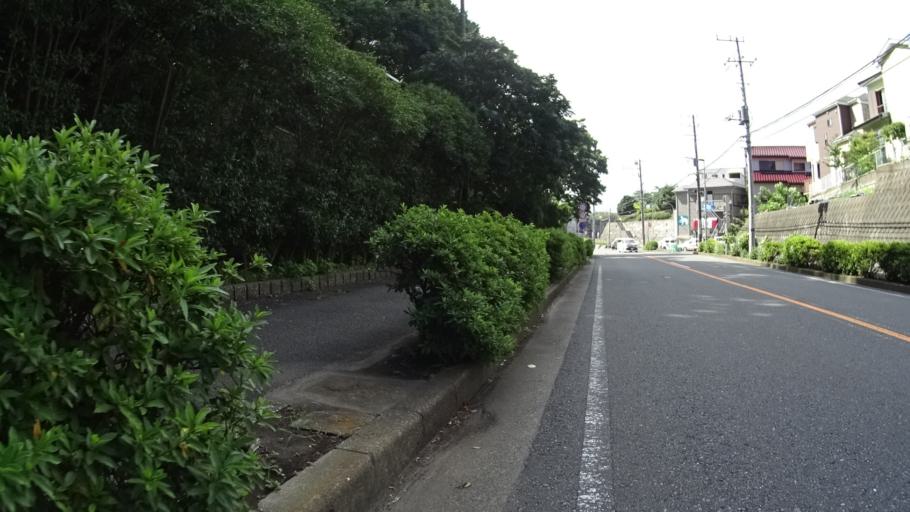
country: JP
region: Kanagawa
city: Yokosuka
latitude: 35.2576
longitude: 139.7082
